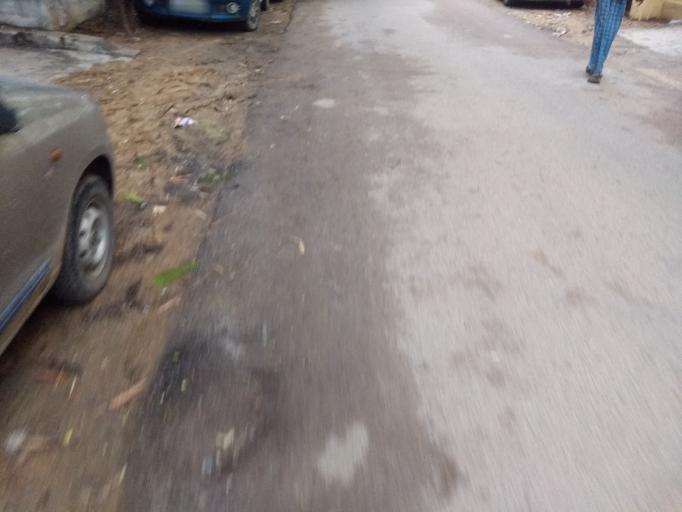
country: IN
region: Telangana
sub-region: Rangareddi
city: Kukatpalli
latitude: 17.4879
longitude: 78.3859
